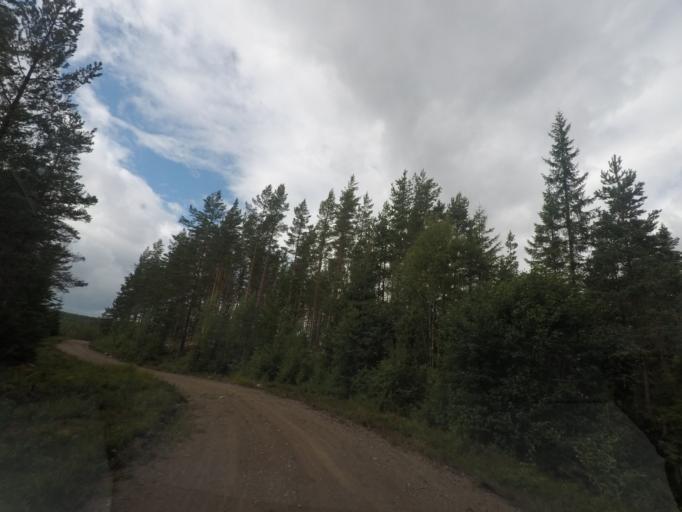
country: SE
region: Vaermland
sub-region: Filipstads Kommun
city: Lesjofors
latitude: 60.1053
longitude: 14.3863
